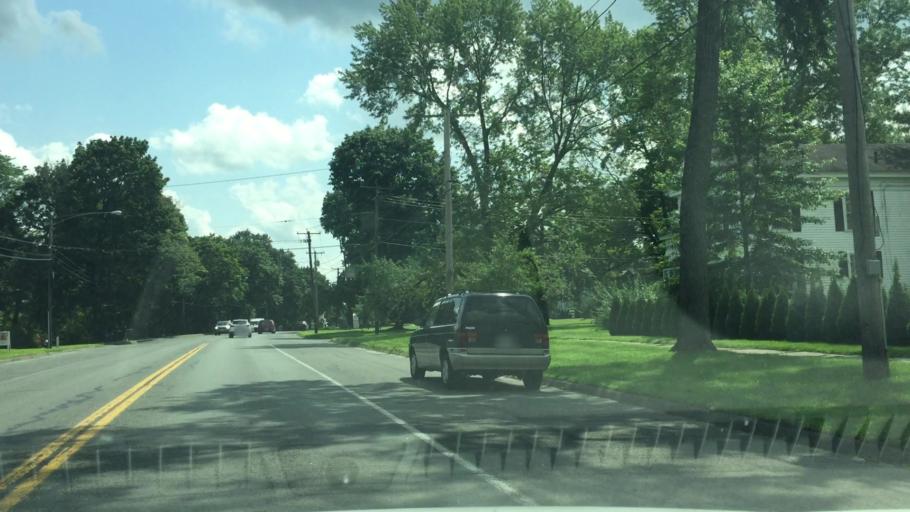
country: US
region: Massachusetts
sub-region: Berkshire County
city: Great Barrington
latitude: 42.1875
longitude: -73.3644
